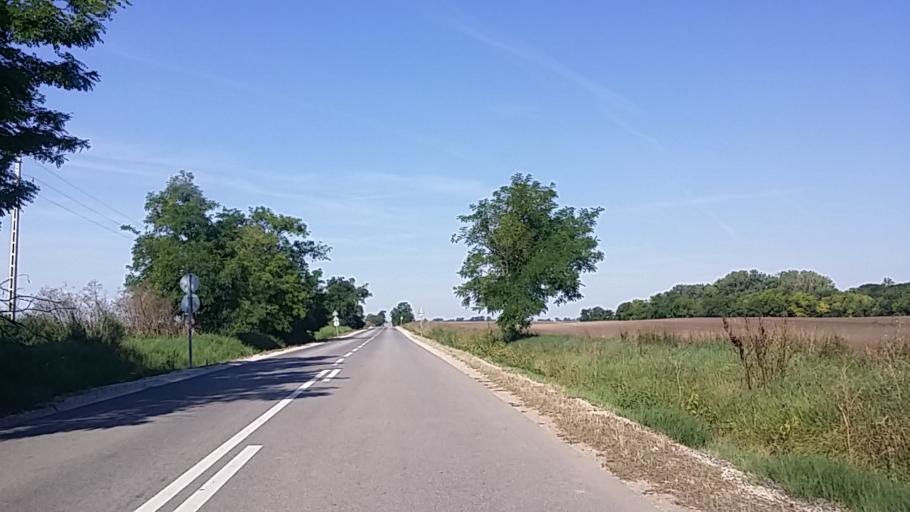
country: HU
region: Fejer
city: Pusztaszabolcs
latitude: 47.1114
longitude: 18.7659
